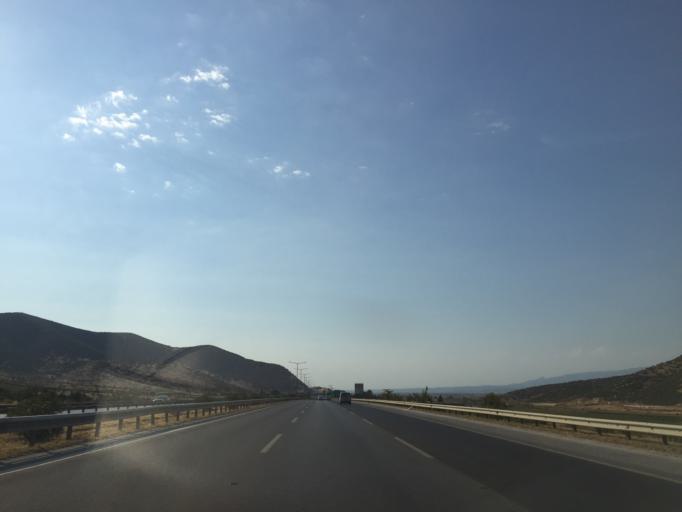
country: TR
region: Izmir
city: Belevi
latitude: 38.0615
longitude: 27.4196
